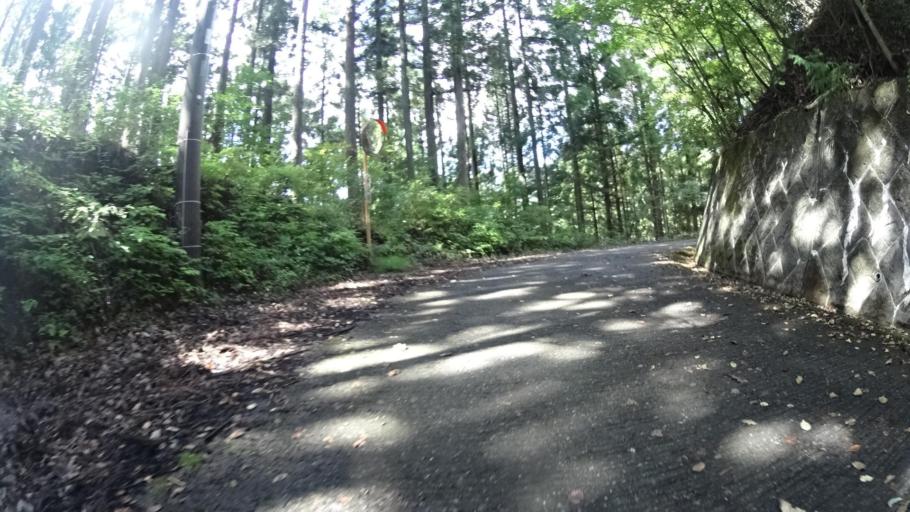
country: JP
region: Yamanashi
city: Uenohara
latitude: 35.7434
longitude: 139.0609
